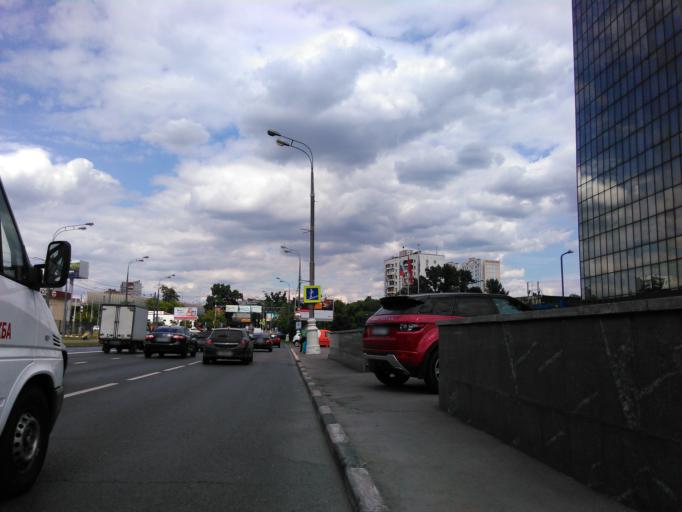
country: RU
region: Moscow
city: Novyye Cheremushki
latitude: 55.6999
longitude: 37.6147
